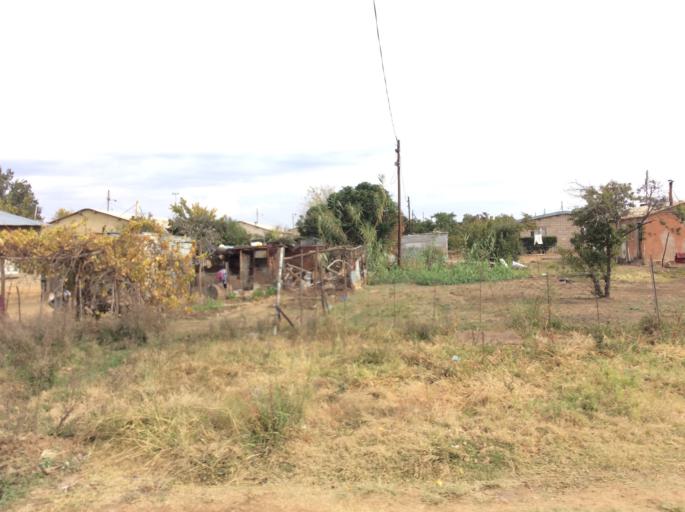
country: LS
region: Mafeteng
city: Mafeteng
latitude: -29.7227
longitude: 27.0107
